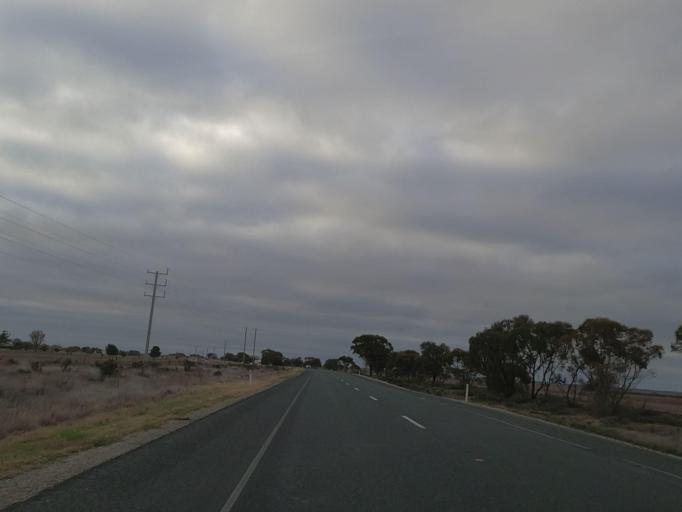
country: AU
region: Victoria
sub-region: Swan Hill
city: Swan Hill
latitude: -35.5862
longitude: 143.7903
